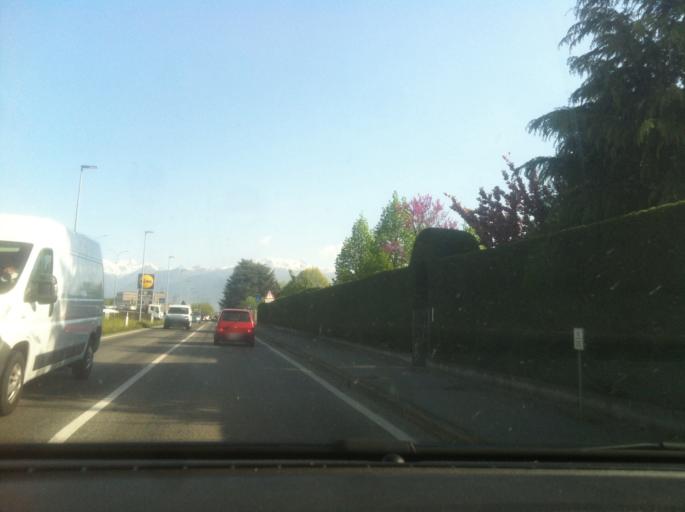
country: IT
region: Piedmont
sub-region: Provincia di Torino
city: Strambino
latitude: 45.3871
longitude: 7.8852
